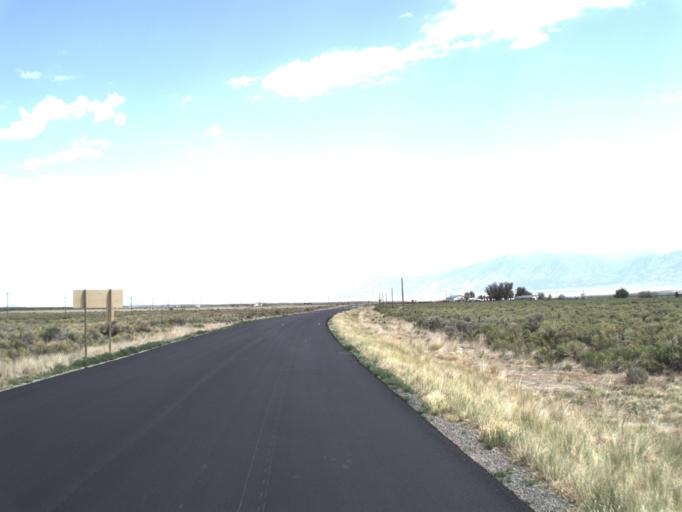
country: US
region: Utah
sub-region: Tooele County
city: Tooele
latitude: 40.1646
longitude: -112.4307
